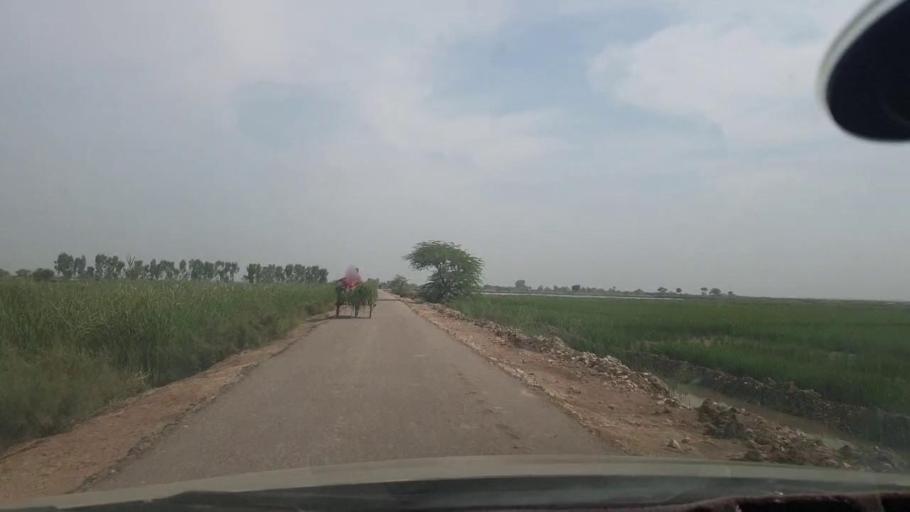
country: PK
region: Sindh
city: Jacobabad
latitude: 28.3066
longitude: 68.4753
